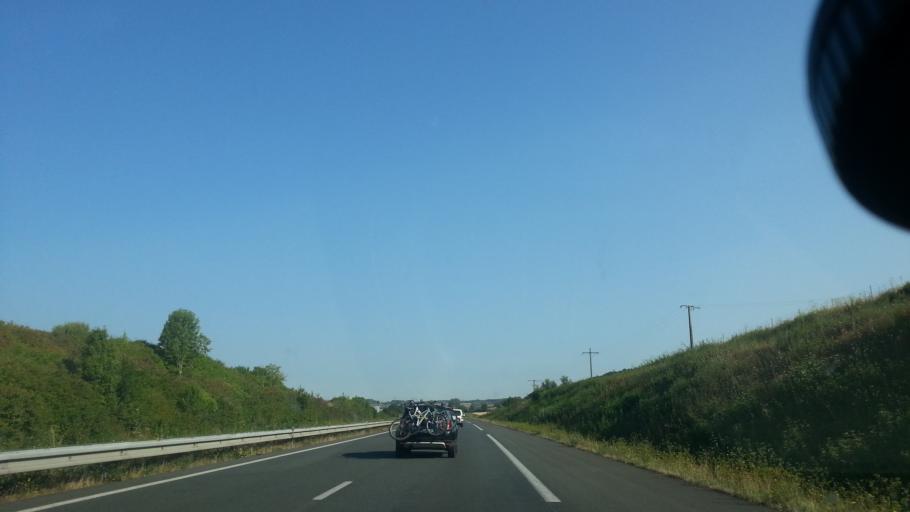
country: FR
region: Poitou-Charentes
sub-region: Departement de la Vienne
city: Antran
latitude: 46.8673
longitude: 0.5234
